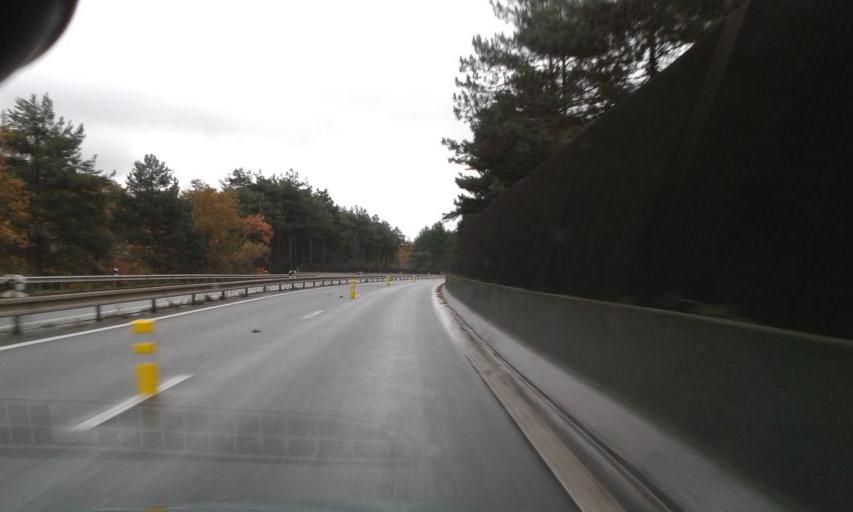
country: FR
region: Centre
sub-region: Departement du Loiret
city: Saran
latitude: 47.9479
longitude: 1.8703
